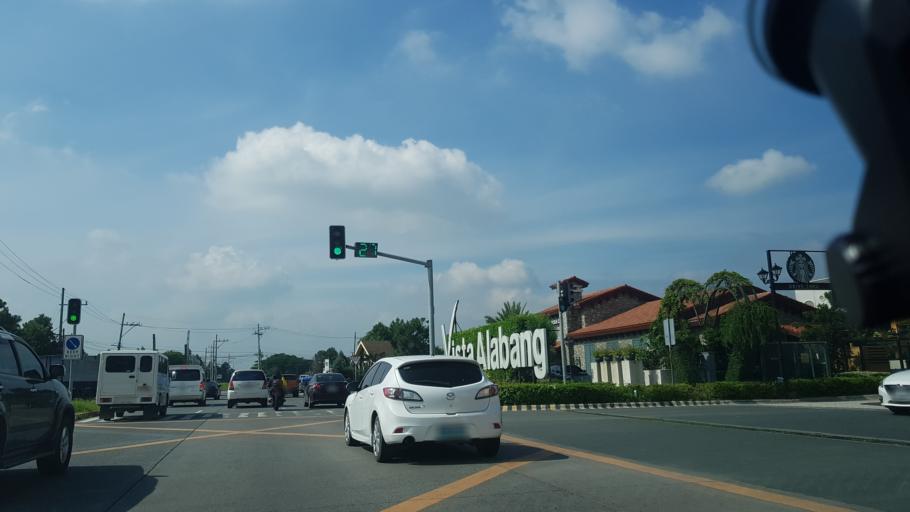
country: PH
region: Calabarzon
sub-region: Province of Laguna
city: San Pedro
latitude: 14.3766
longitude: 121.0129
